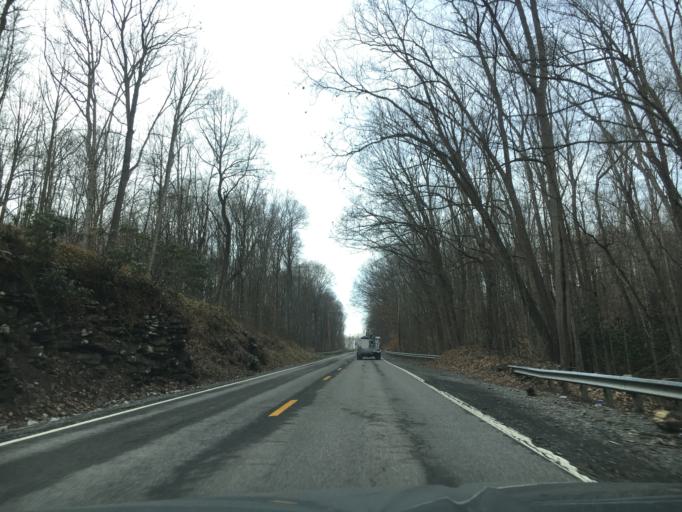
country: US
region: West Virginia
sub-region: Fayette County
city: Fayetteville
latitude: 38.0494
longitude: -80.9466
